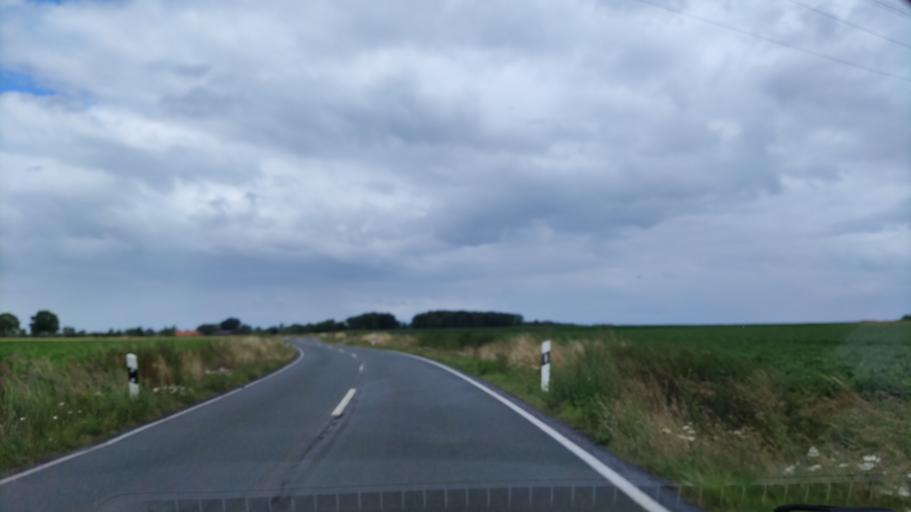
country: DE
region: North Rhine-Westphalia
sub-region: Regierungsbezirk Arnsberg
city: Welver
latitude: 51.6263
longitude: 8.0128
